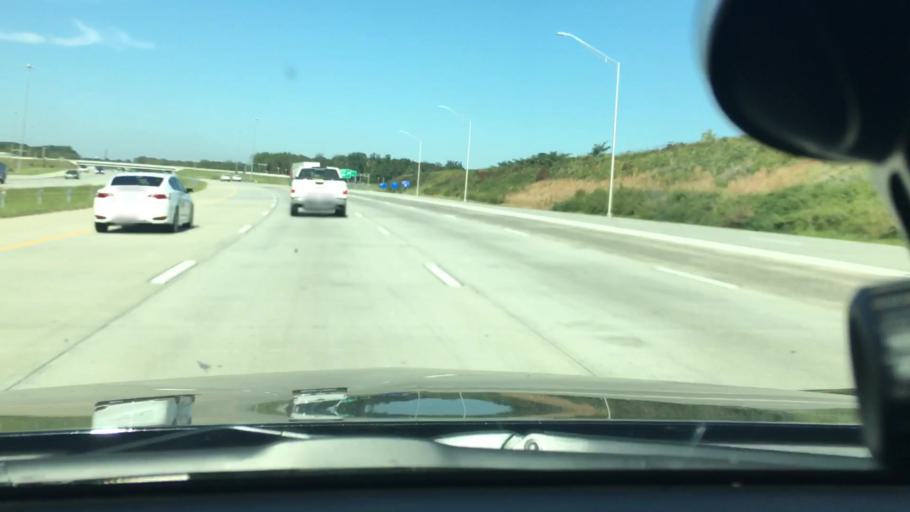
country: US
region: North Carolina
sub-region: Cabarrus County
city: Harrisburg
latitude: 35.3595
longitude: -80.7433
